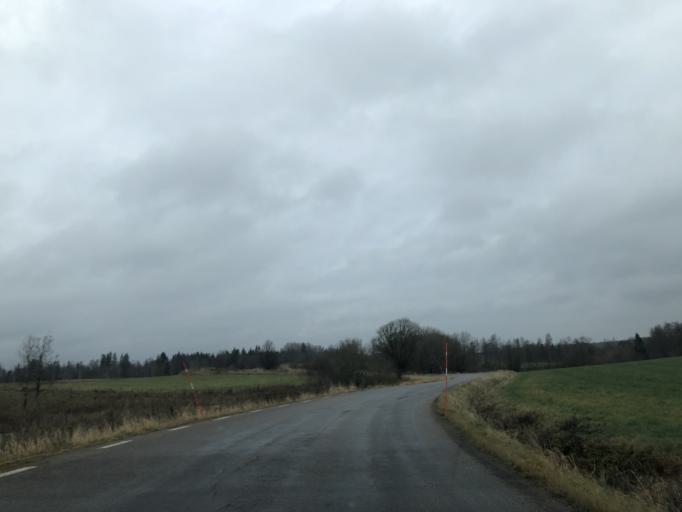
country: SE
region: Vaestra Goetaland
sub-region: Ulricehamns Kommun
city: Ulricehamn
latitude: 57.8846
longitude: 13.5128
